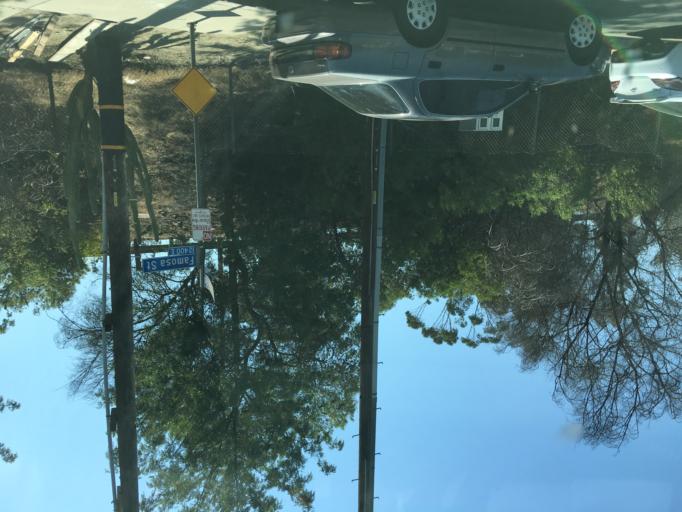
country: US
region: California
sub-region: Los Angeles County
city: South El Monte
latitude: 34.0336
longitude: -118.0300
